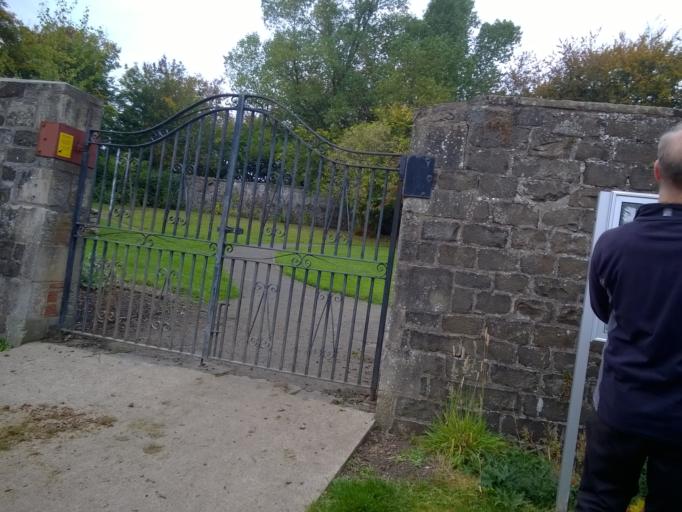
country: GB
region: Scotland
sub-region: West Lothian
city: Livingston
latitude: 55.8934
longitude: -3.5169
